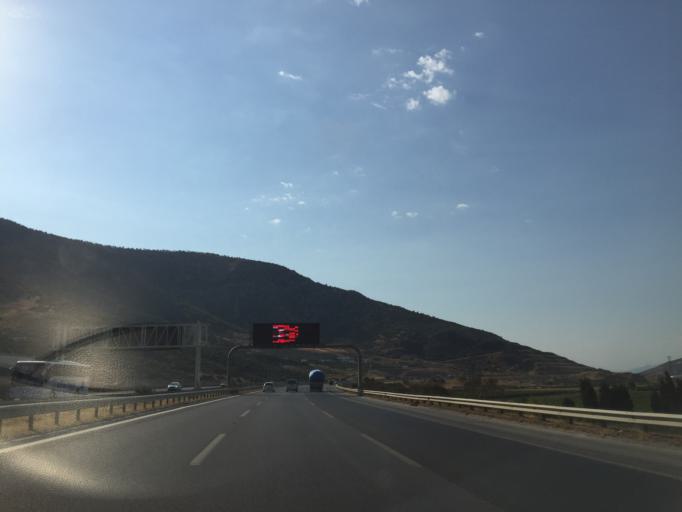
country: TR
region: Izmir
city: Belevi
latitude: 38.0288
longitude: 27.4352
